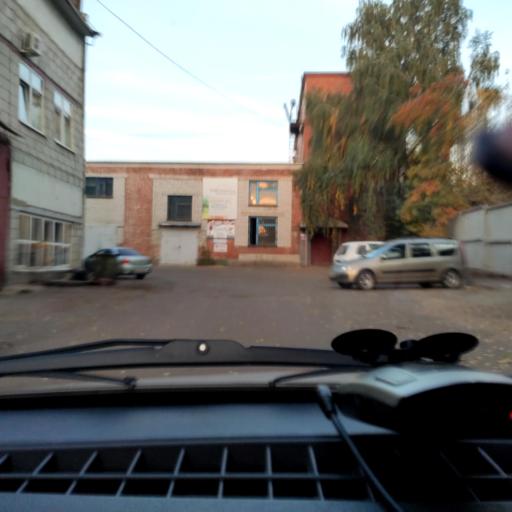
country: RU
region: Voronezj
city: Voronezh
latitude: 51.6610
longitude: 39.1379
